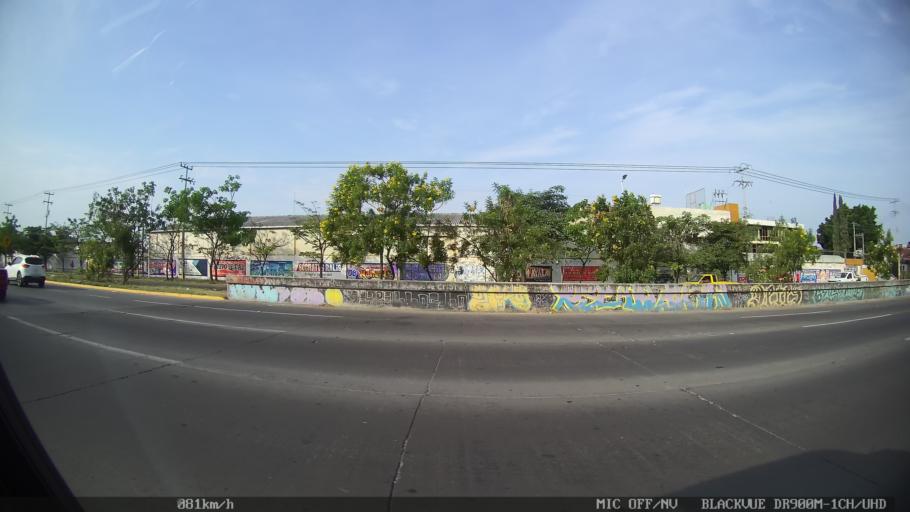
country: MX
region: Jalisco
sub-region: Zapopan
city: Zapopan
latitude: 20.7195
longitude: -103.3136
